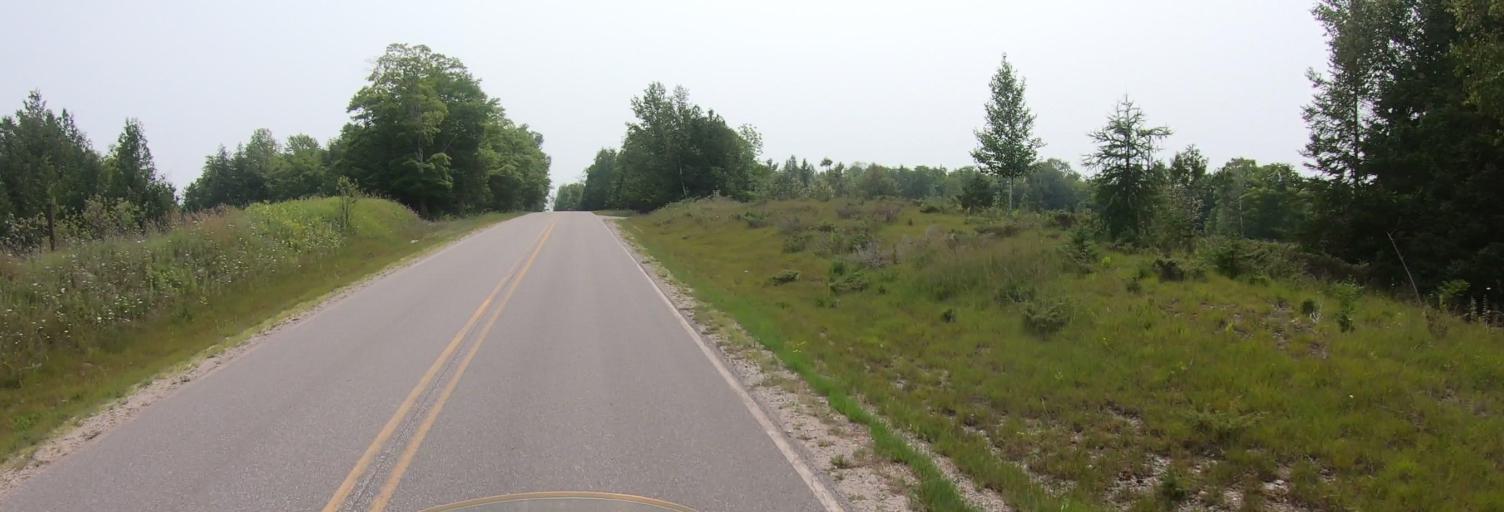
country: CA
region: Ontario
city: Thessalon
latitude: 45.9975
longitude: -83.7388
